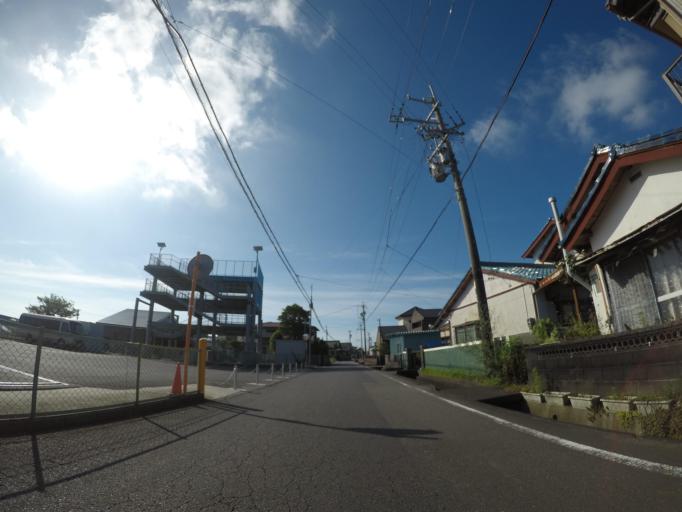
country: JP
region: Shizuoka
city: Fujieda
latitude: 34.7874
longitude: 138.2820
